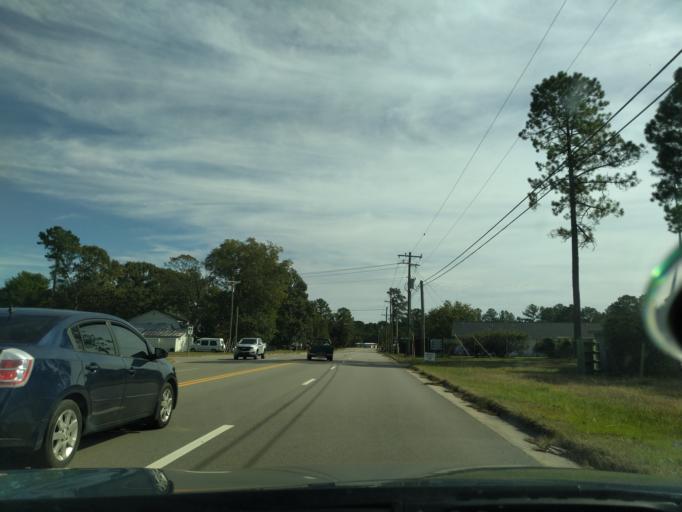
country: US
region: North Carolina
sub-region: Beaufort County
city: River Road
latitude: 35.5219
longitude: -77.0077
